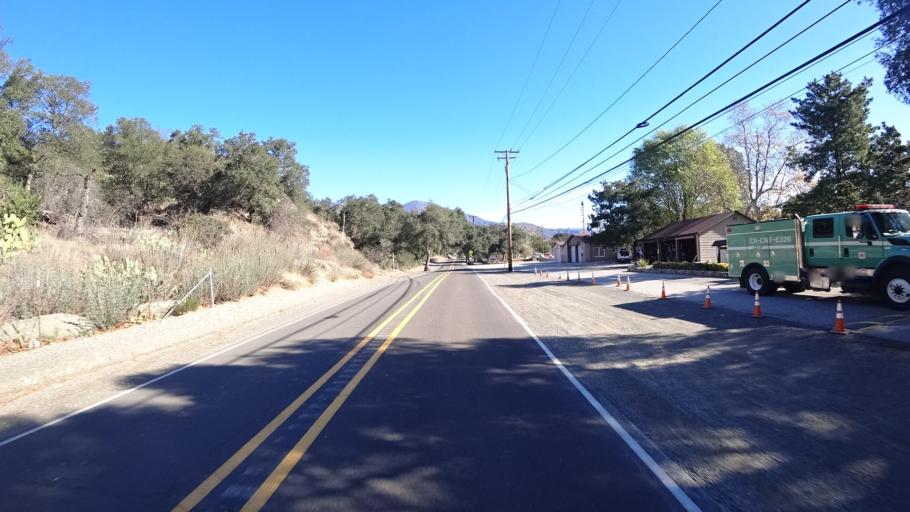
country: US
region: California
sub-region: Orange County
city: Trabuco Canyon
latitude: 33.6582
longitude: -117.5926
